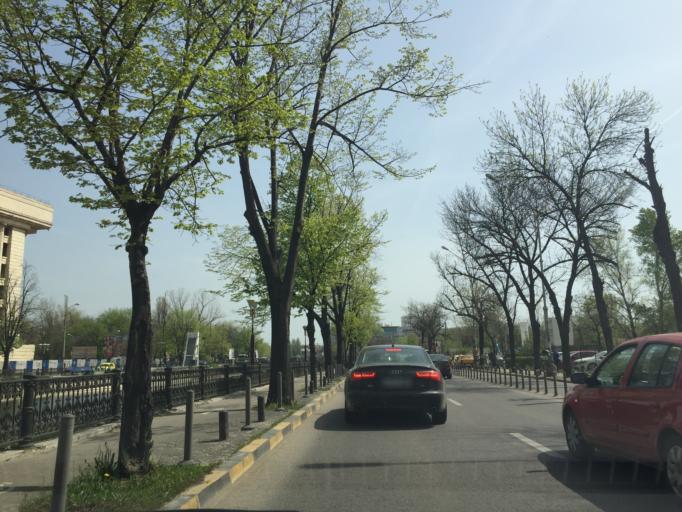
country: RO
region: Bucuresti
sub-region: Municipiul Bucuresti
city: Bucuresti
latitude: 44.4366
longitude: 26.0730
